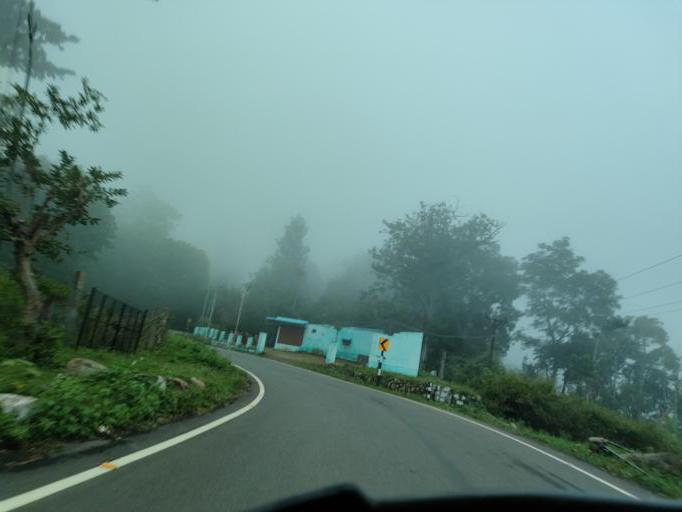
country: IN
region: Tamil Nadu
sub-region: Dindigul
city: Ayakudi
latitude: 10.3561
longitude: 77.5632
